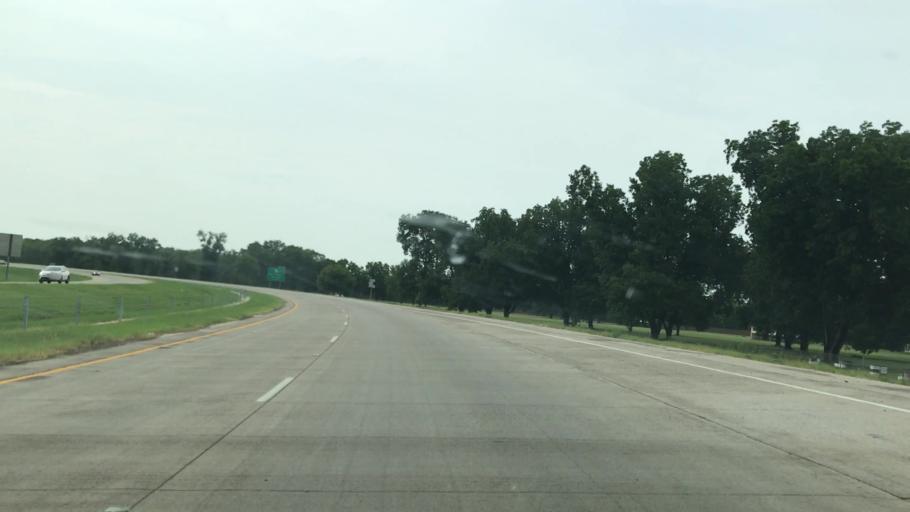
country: US
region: Louisiana
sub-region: Bossier Parish
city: Bossier City
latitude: 32.4064
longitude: -93.7148
